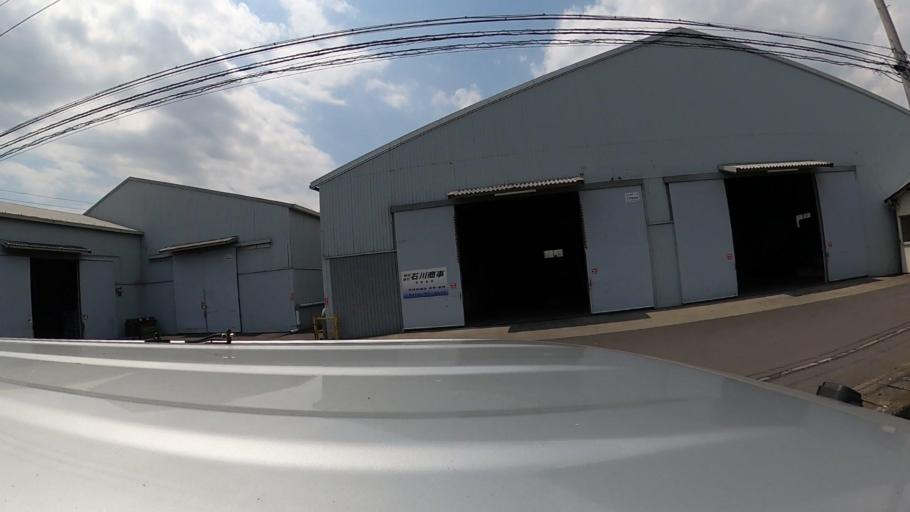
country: JP
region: Kanagawa
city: Chigasaki
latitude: 35.3870
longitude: 139.4021
